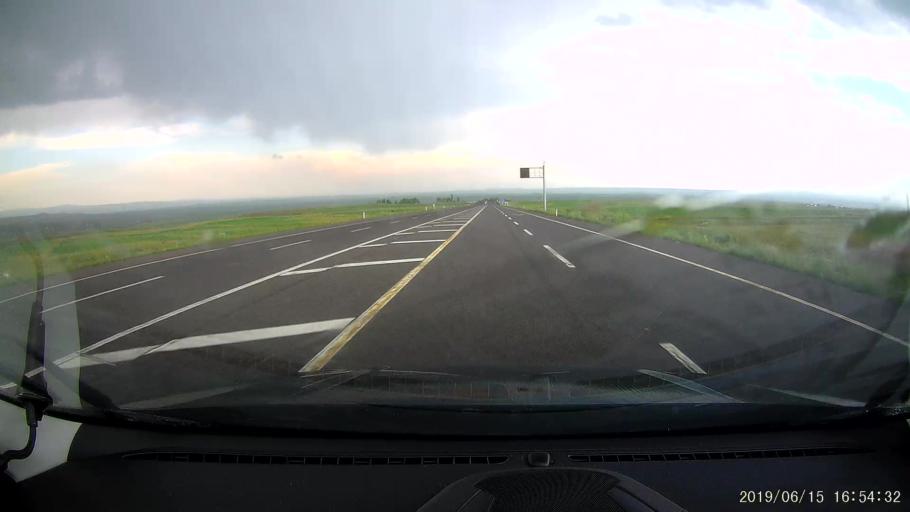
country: TR
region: Kars
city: Susuz
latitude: 40.7898
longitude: 43.1267
